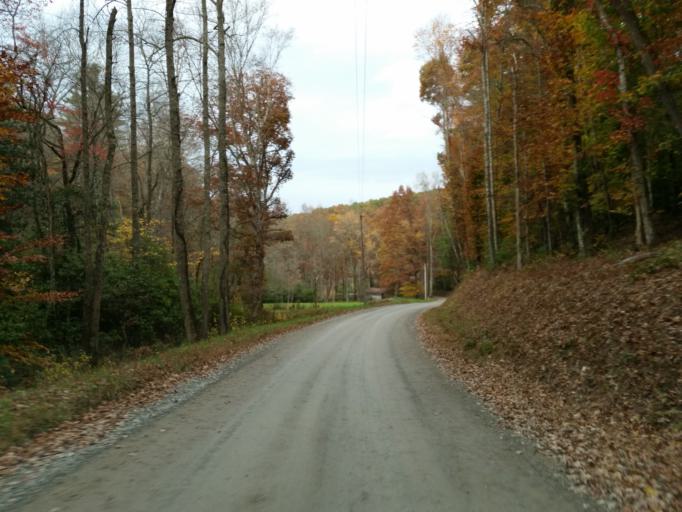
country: US
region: Georgia
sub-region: Fannin County
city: Blue Ridge
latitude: 34.7215
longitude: -84.2164
